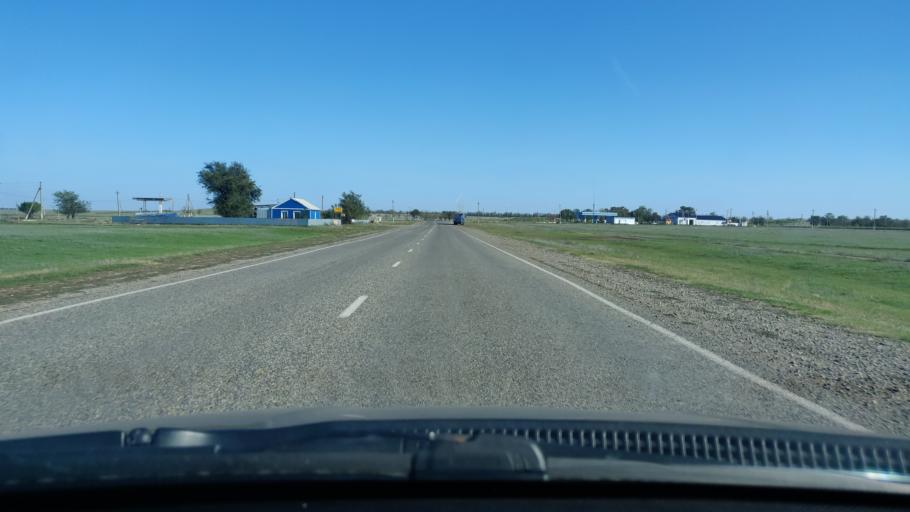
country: RU
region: Stavropol'skiy
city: Letnyaya Stavka
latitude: 45.3740
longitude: 43.6881
